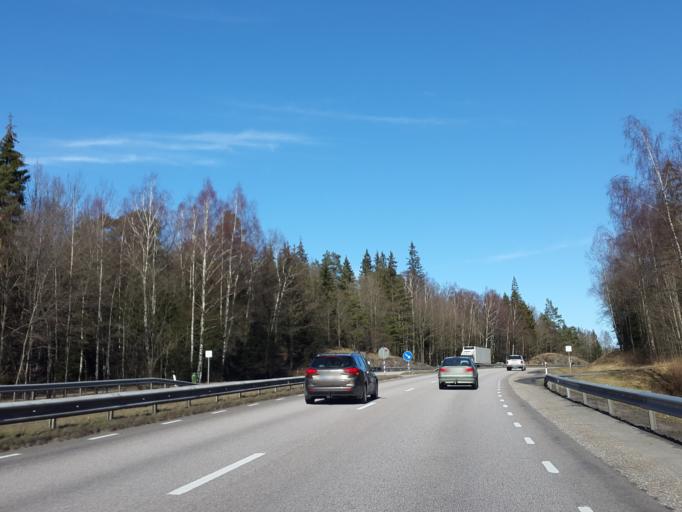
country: SE
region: Vaestra Goetaland
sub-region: Alingsas Kommun
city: Ingared
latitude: 57.8349
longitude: 12.4387
